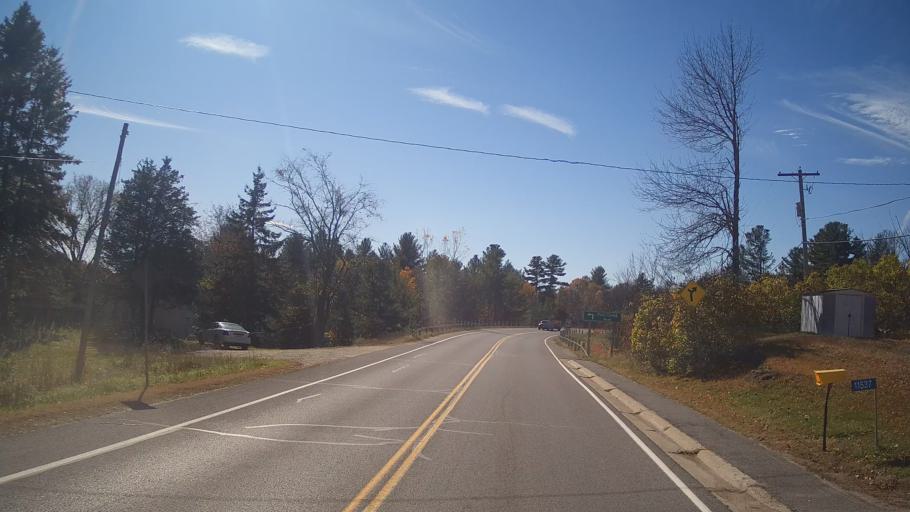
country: CA
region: Ontario
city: Kingston
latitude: 44.6612
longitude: -76.6816
